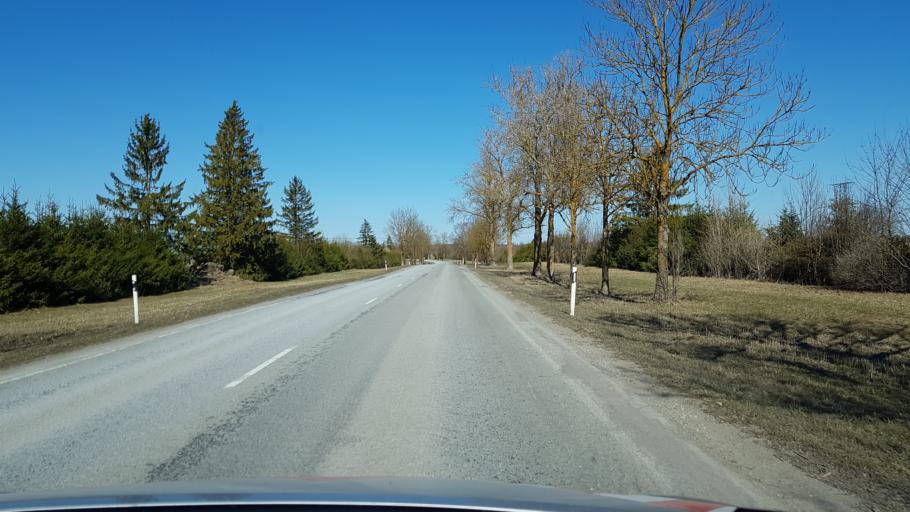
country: EE
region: Laeaene-Virumaa
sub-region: Rakvere linn
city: Rakvere
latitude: 59.3751
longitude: 26.3880
